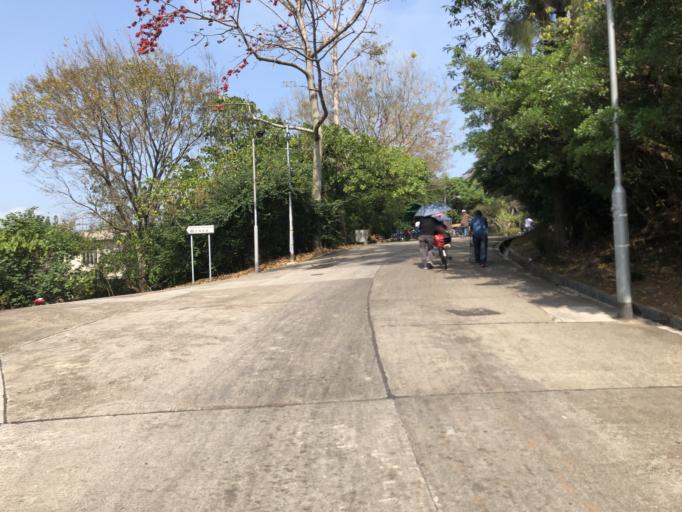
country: HK
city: Yung Shue Wan
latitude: 22.2123
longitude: 114.0241
